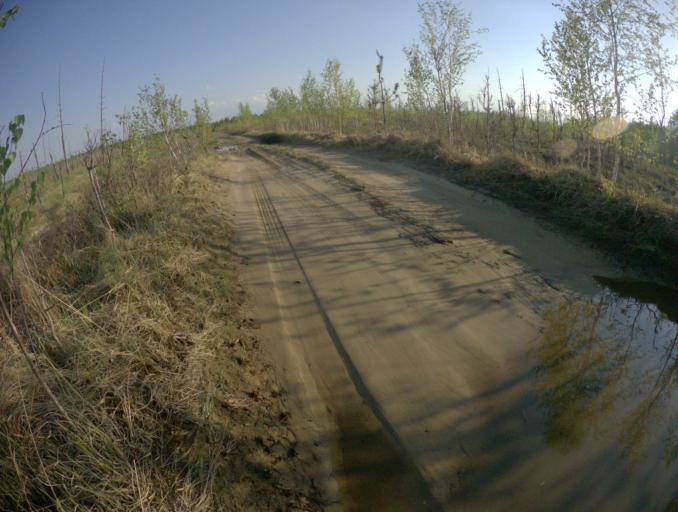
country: RU
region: Vladimir
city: Vyazniki
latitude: 56.3851
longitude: 42.1727
